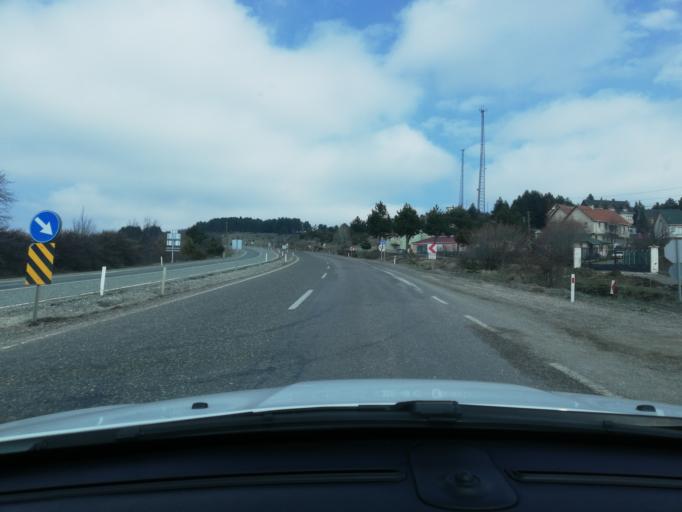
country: TR
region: Kastamonu
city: Kuzyaka
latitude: 41.2348
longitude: 33.7929
